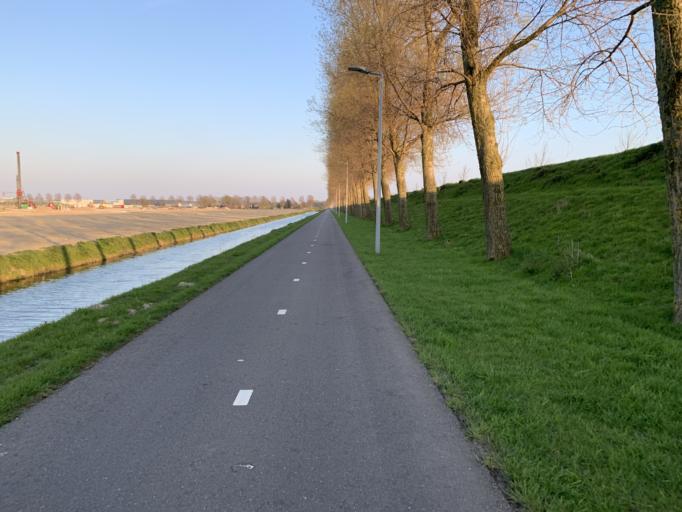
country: NL
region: North Holland
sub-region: Gemeente Haarlemmermeer
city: Hoofddorp
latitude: 52.2782
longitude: 4.7193
